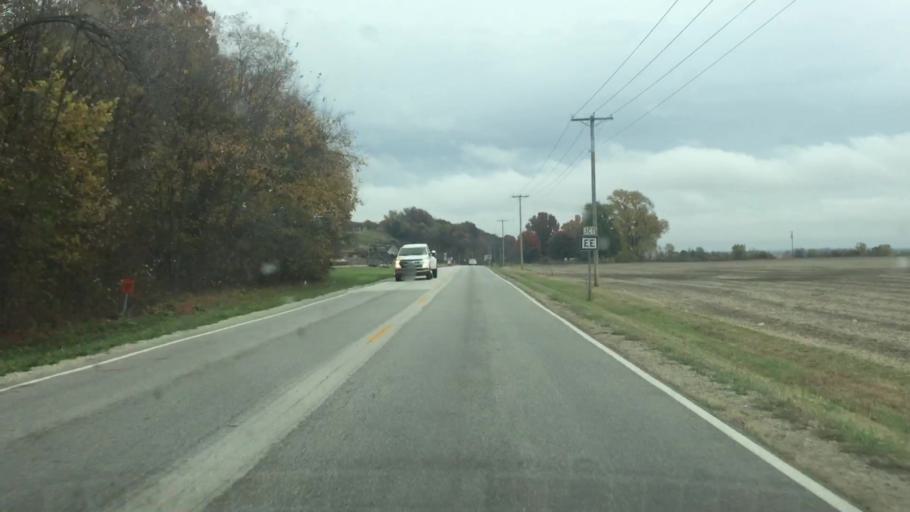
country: US
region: Missouri
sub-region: Gasconade County
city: Hermann
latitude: 38.7201
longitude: -91.5100
